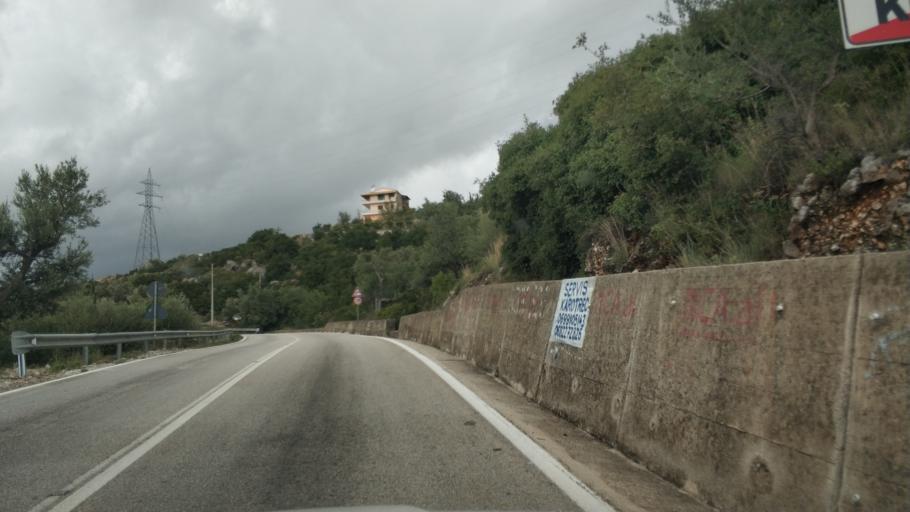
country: AL
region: Vlore
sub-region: Rrethi i Vlores
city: Vranisht
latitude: 40.1587
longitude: 19.6297
